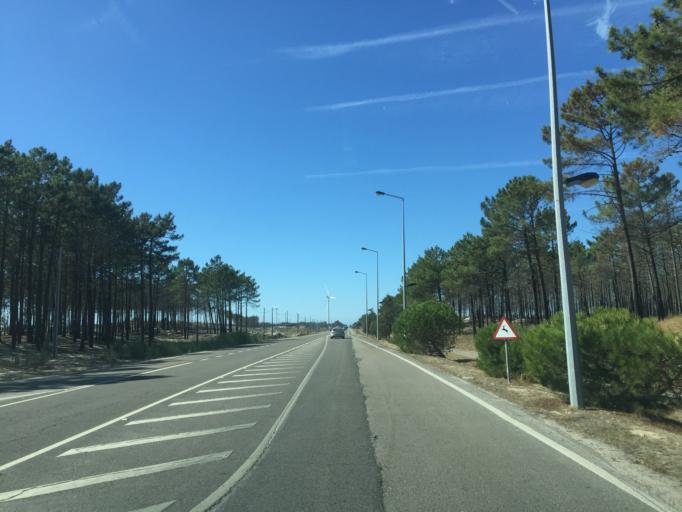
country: PT
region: Coimbra
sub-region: Mira
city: Mira
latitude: 40.3226
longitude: -8.7889
